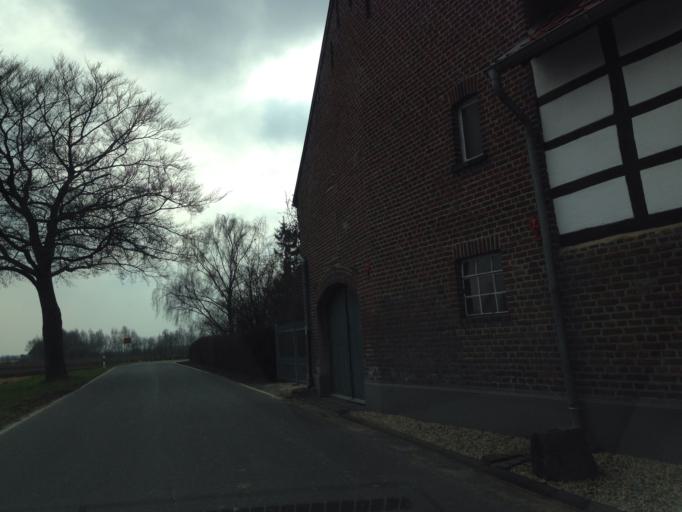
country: DE
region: North Rhine-Westphalia
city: Huckelhoven
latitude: 51.0874
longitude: 6.2584
